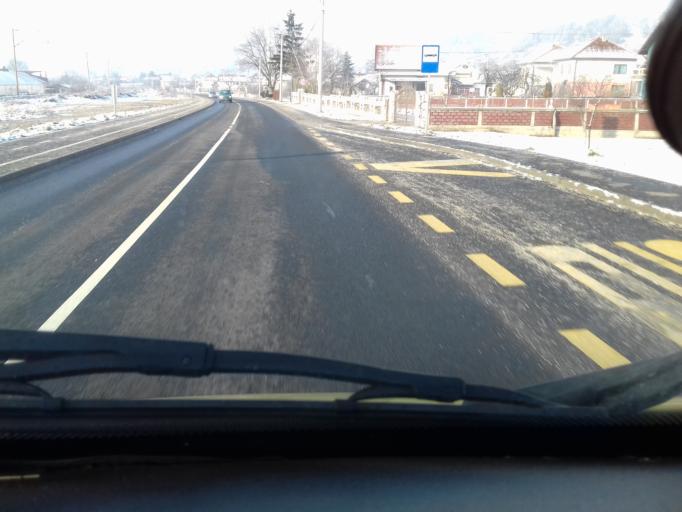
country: BA
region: Federation of Bosnia and Herzegovina
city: Mahala
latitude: 43.9834
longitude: 18.2388
